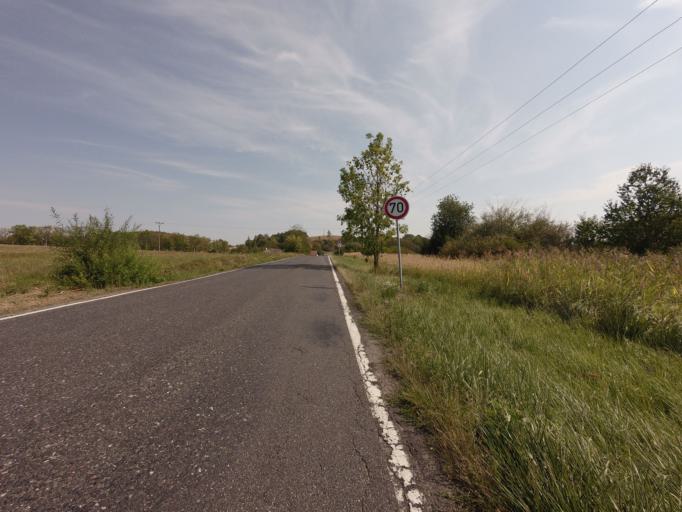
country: CZ
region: Central Bohemia
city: Petrovice
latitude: 49.5739
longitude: 14.3733
